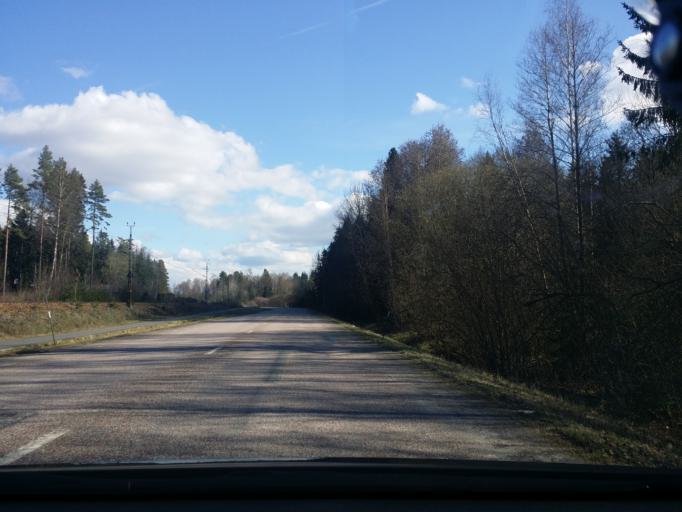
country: SE
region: Vaestmanland
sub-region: Sala Kommun
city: Sala
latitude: 59.9436
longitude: 16.5492
